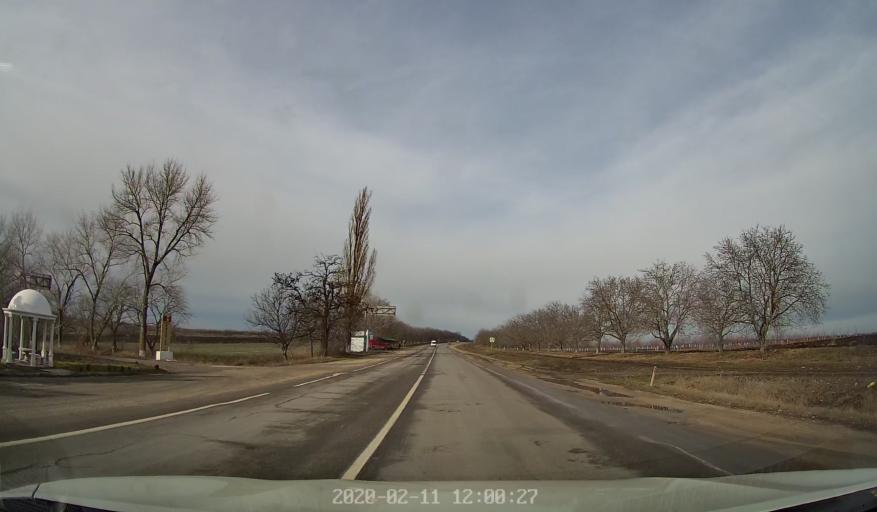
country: MD
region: Riscani
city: Riscani
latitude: 47.9277
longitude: 27.6426
